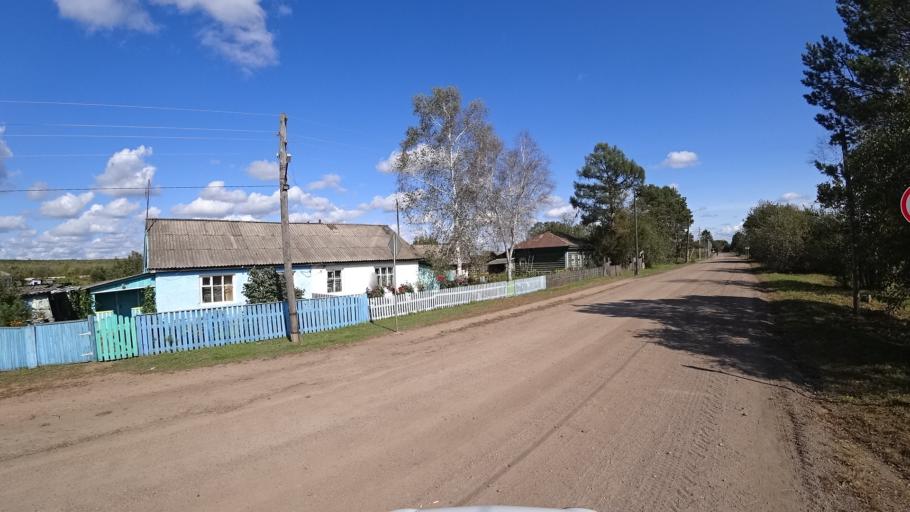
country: RU
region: Amur
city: Arkhara
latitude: 49.4022
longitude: 130.1447
